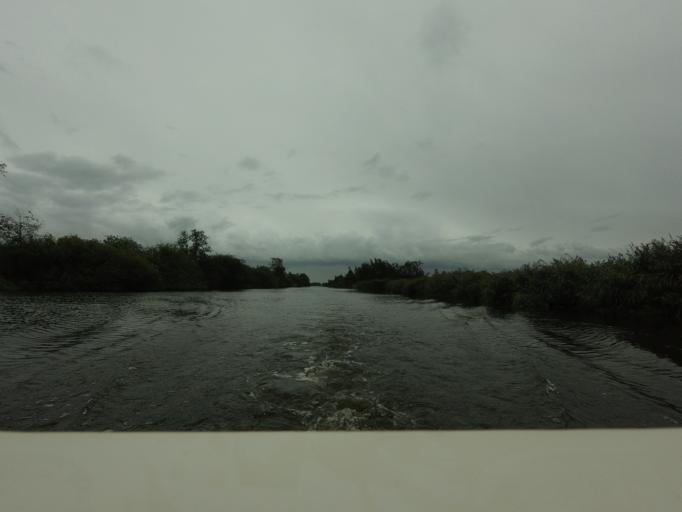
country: NL
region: Friesland
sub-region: Gemeente Boarnsterhim
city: Warten
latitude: 53.1196
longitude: 5.9305
